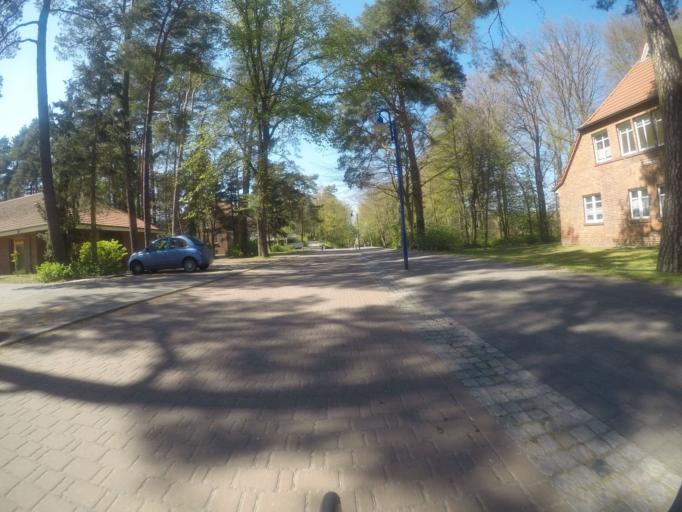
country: DE
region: Brandenburg
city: Rudnitz
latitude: 52.7282
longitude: 13.5955
